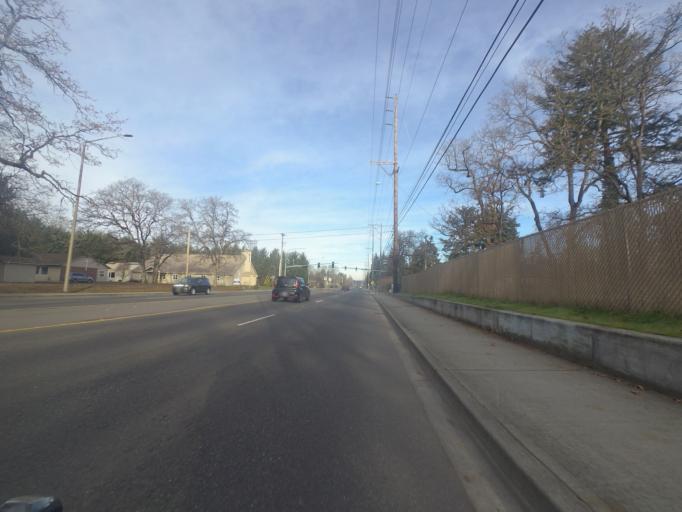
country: US
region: Washington
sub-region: Pierce County
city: Lakewood
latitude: 47.1787
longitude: -122.5179
